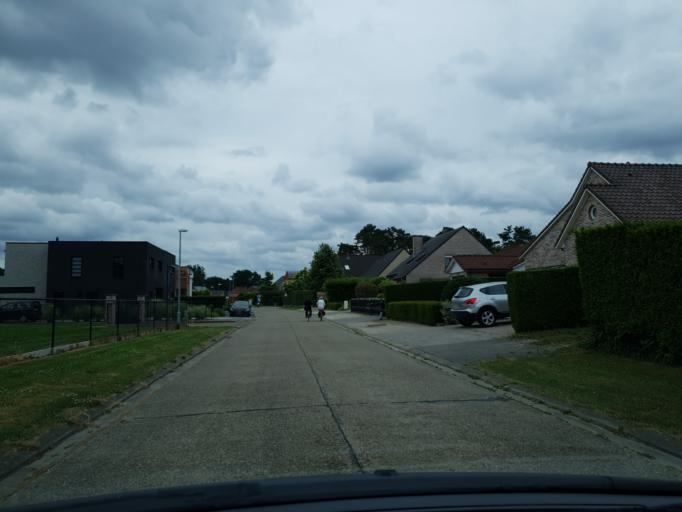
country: BE
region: Flanders
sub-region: Provincie Antwerpen
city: Westerlo
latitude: 51.0970
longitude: 4.9152
